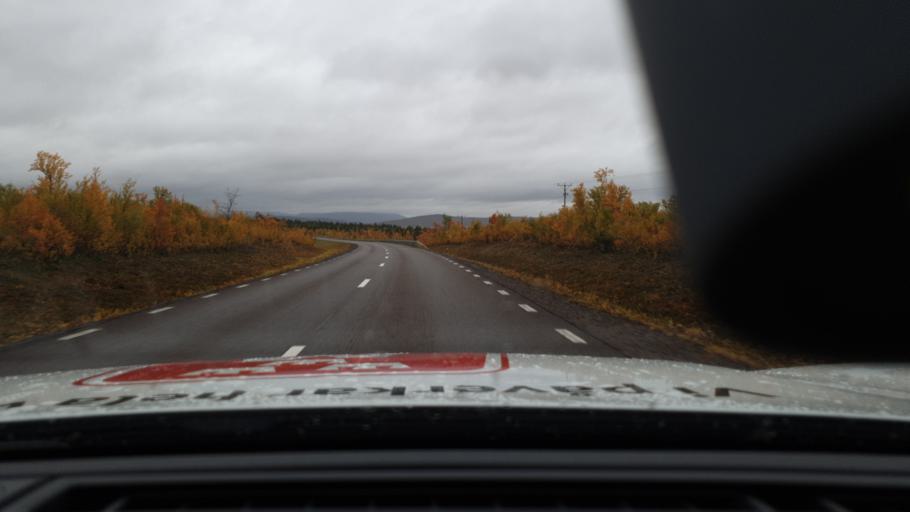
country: SE
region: Norrbotten
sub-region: Kiruna Kommun
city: Kiruna
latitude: 67.9851
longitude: 19.9407
